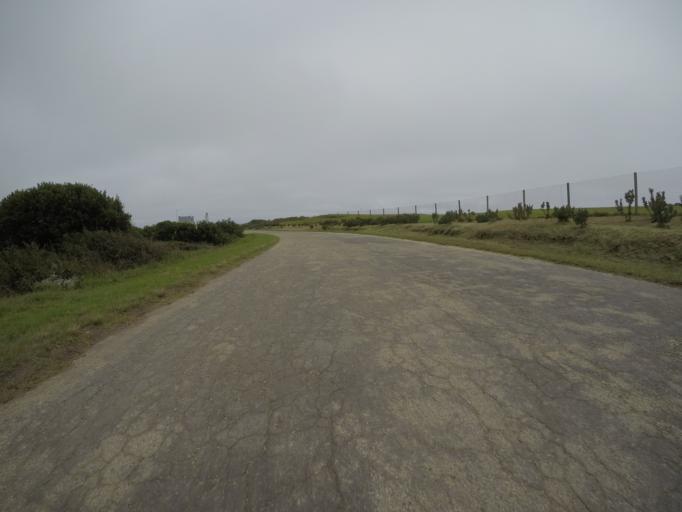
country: ZA
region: Eastern Cape
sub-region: Cacadu District Municipality
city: Kareedouw
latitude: -34.0720
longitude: 24.2326
